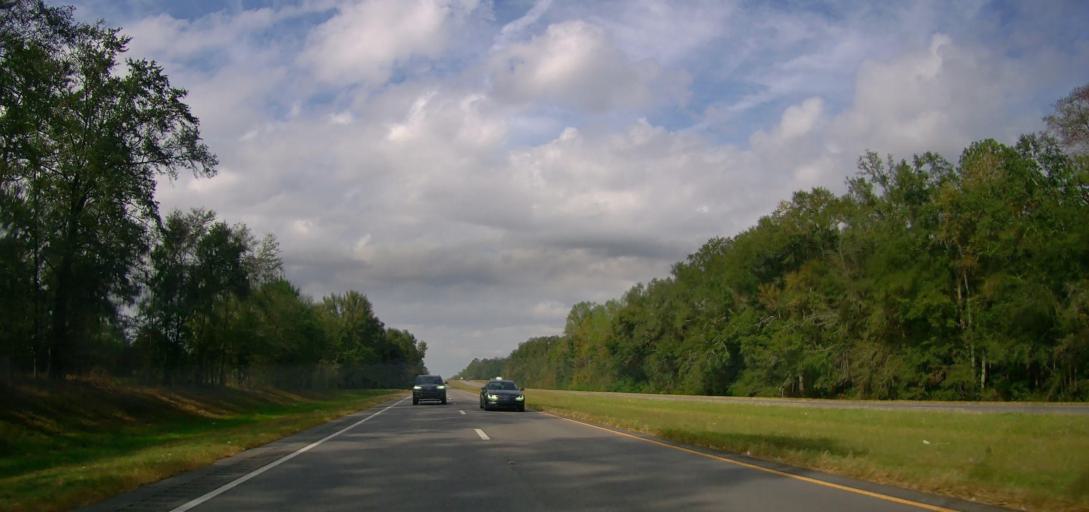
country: US
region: Georgia
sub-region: Thomas County
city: Meigs
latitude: 31.0041
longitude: -84.0499
